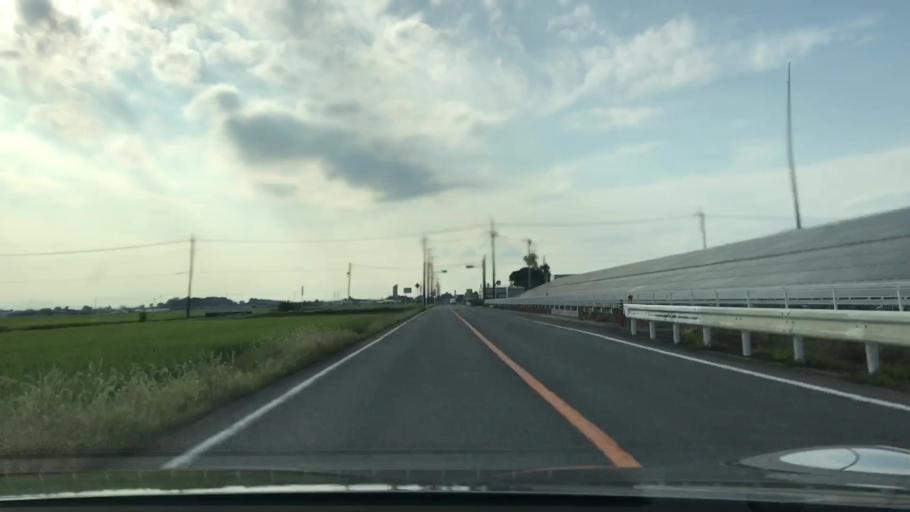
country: JP
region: Saitama
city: Gyoda
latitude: 36.2097
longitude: 139.4614
